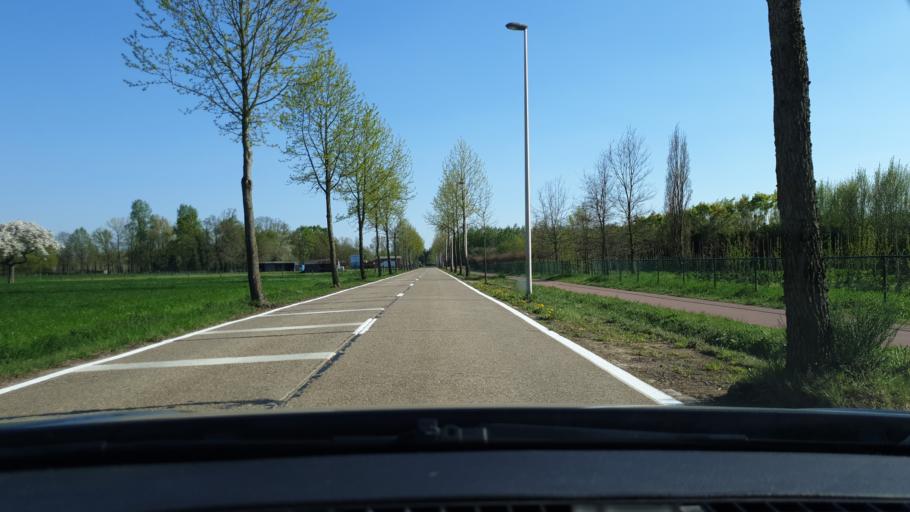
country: BE
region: Flanders
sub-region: Provincie Antwerpen
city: Laakdal
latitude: 51.0918
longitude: 5.0161
